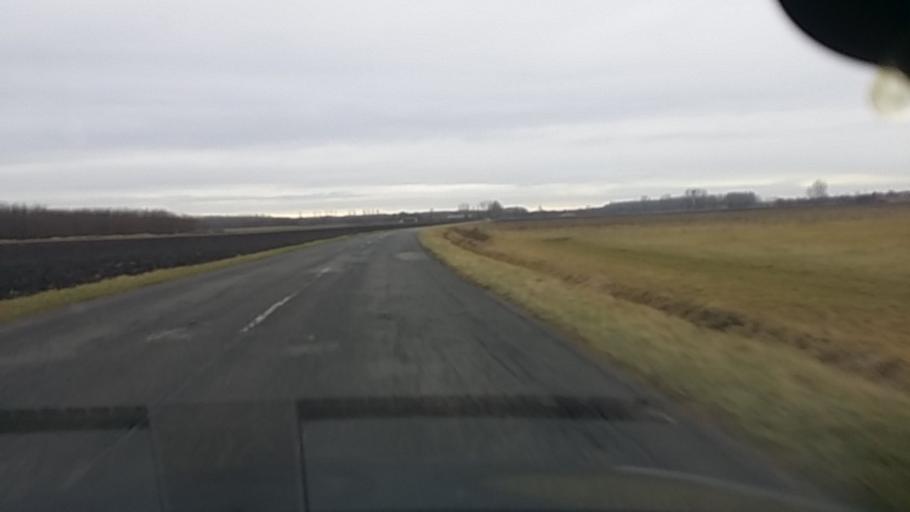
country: HU
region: Szabolcs-Szatmar-Bereg
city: Nyirbogdany
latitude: 48.0500
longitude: 21.8624
